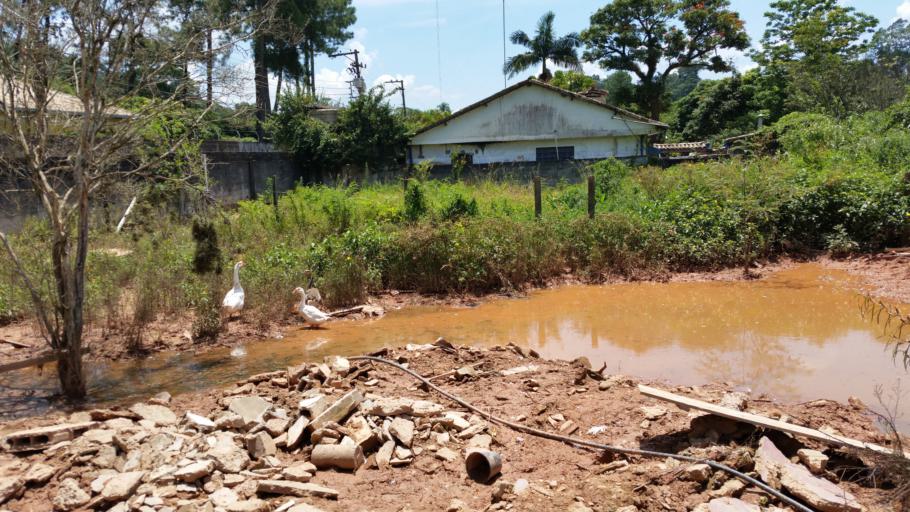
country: BR
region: Sao Paulo
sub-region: Guarulhos
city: Guarulhos
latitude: -23.4298
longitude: -46.5982
